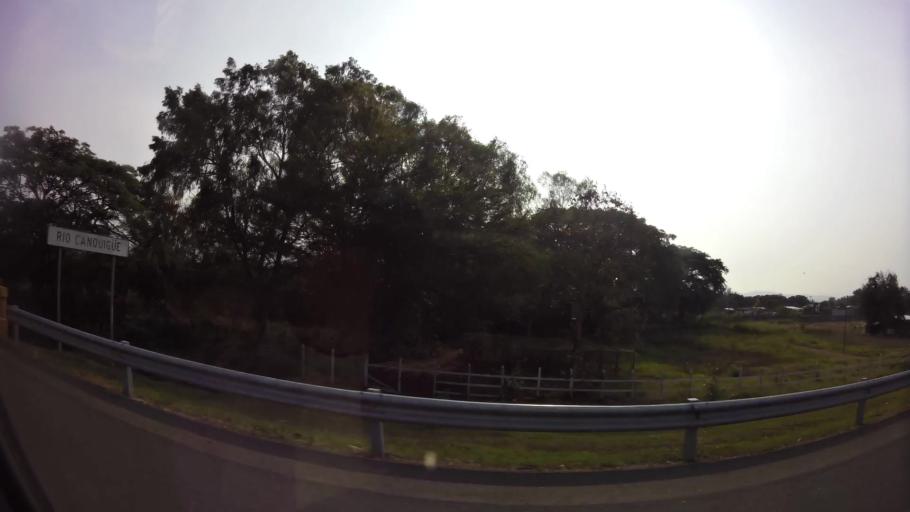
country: HN
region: La Paz
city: Yarumela
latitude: 14.3766
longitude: -87.6077
